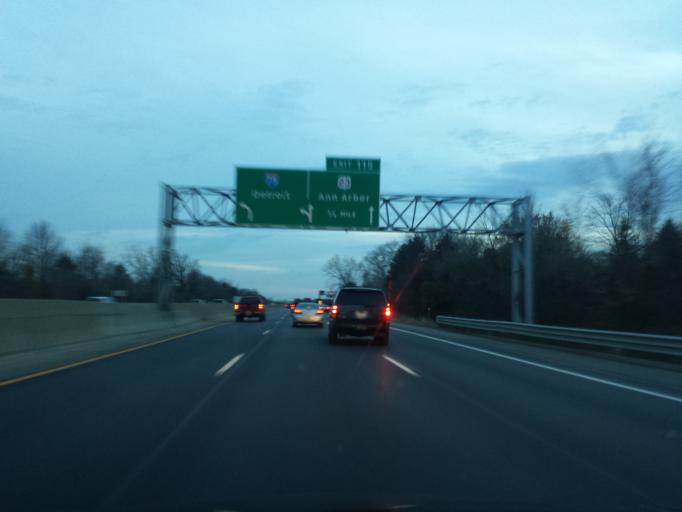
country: US
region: Michigan
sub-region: Genesee County
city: Flint
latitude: 42.9667
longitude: -83.7256
